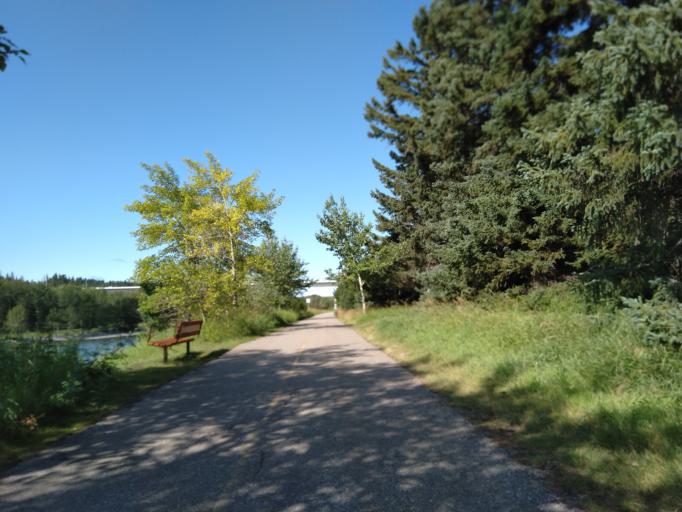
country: CA
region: Alberta
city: Calgary
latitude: 51.0998
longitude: -114.2245
